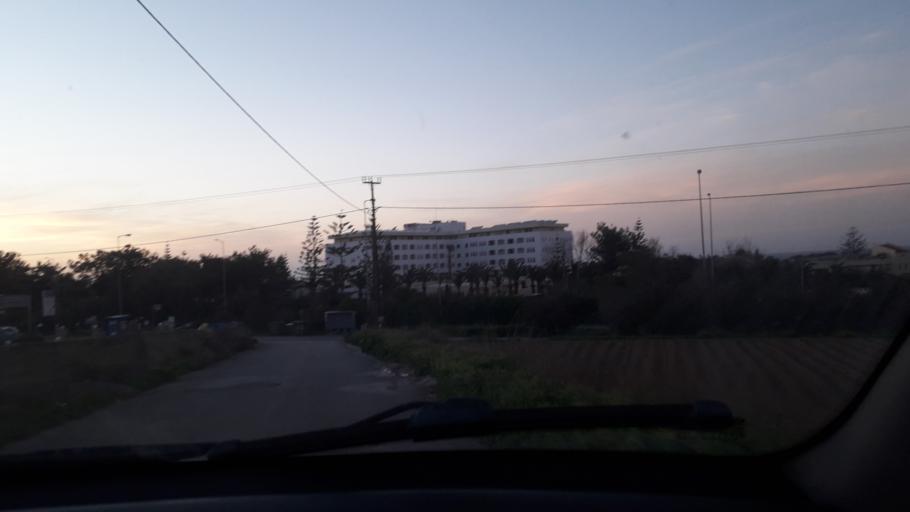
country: GR
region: Crete
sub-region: Nomos Rethymnis
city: Panormos
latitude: 35.3886
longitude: 24.6091
